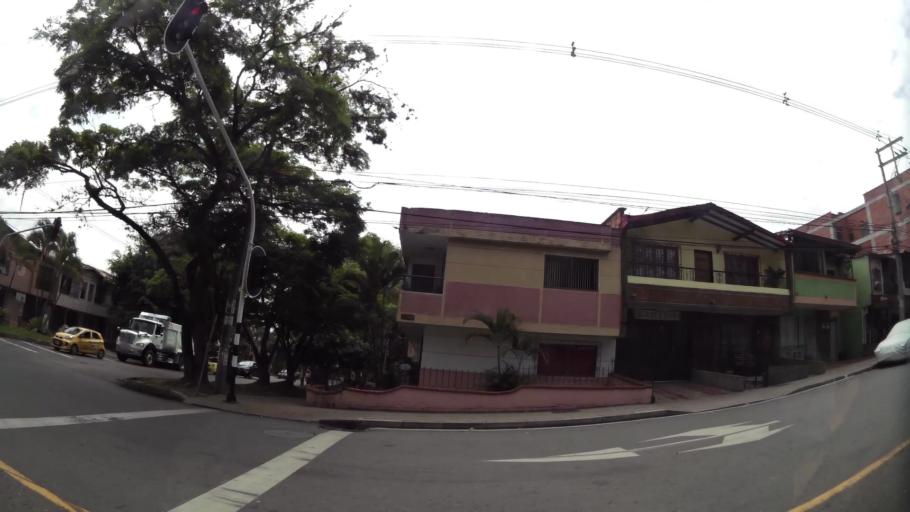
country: CO
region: Antioquia
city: Medellin
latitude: 6.2471
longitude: -75.6158
